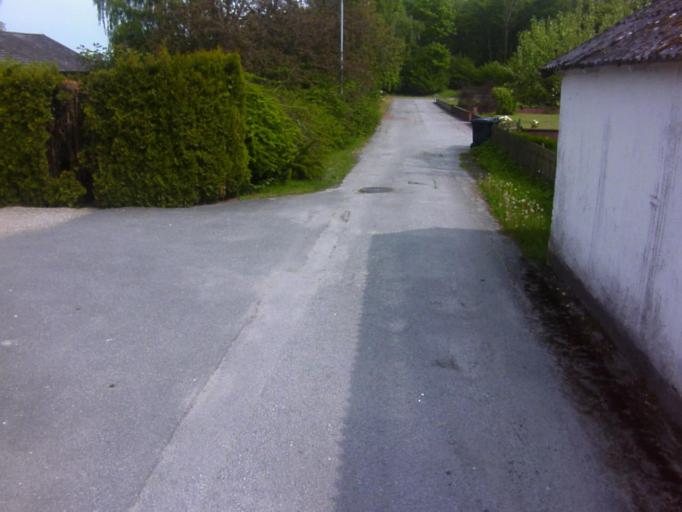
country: SE
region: Blekinge
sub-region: Karlshamns Kommun
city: Morrum
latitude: 56.0394
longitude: 14.7610
